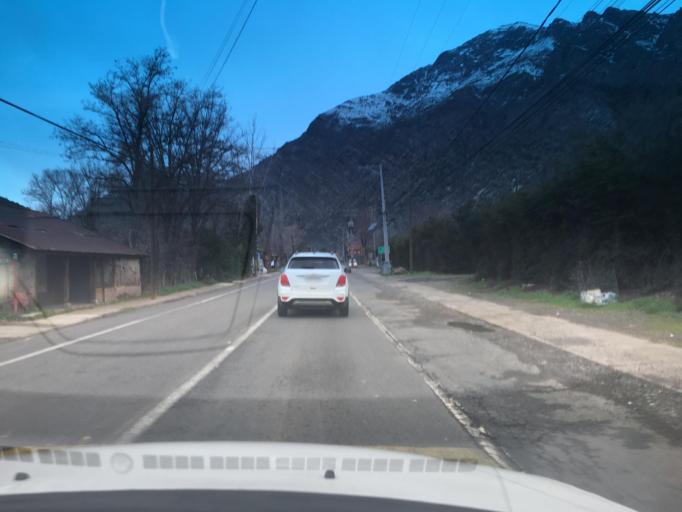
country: CL
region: Santiago Metropolitan
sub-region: Provincia de Cordillera
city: Puente Alto
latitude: -33.7152
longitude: -70.3315
